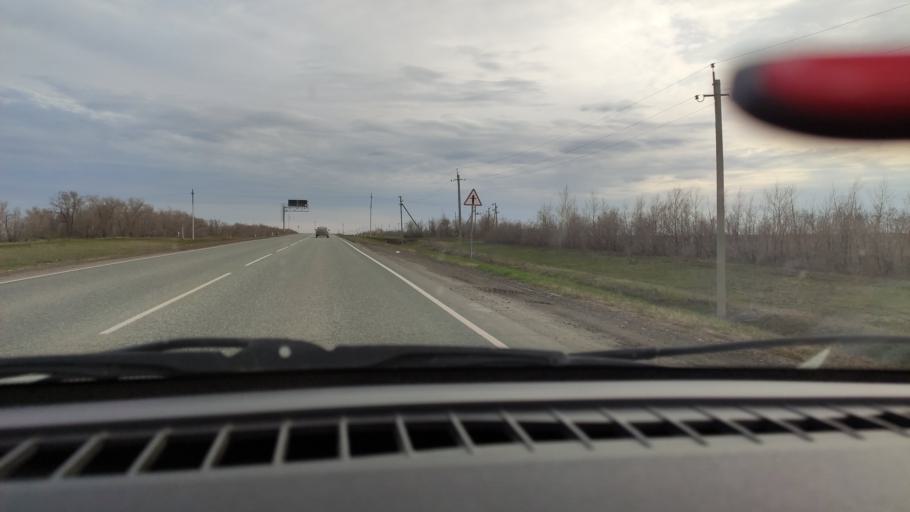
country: RU
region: Orenburg
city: Tatarskaya Kargala
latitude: 52.0010
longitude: 55.1979
